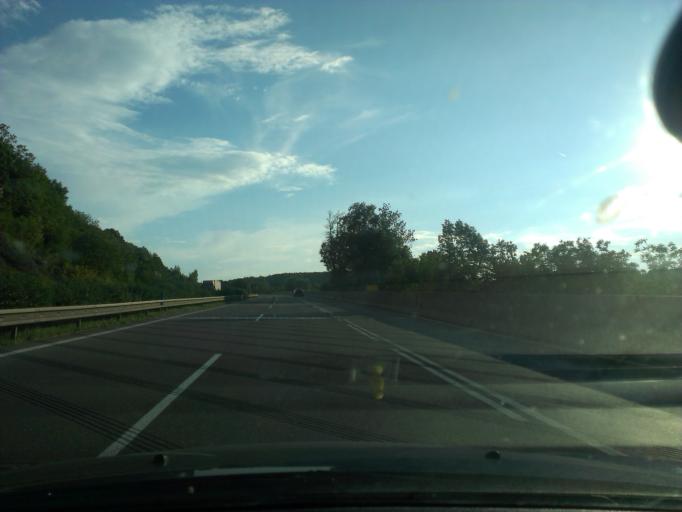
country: SK
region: Trenciansky
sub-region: Okres Trencin
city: Trencin
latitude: 48.9222
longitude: 18.0730
